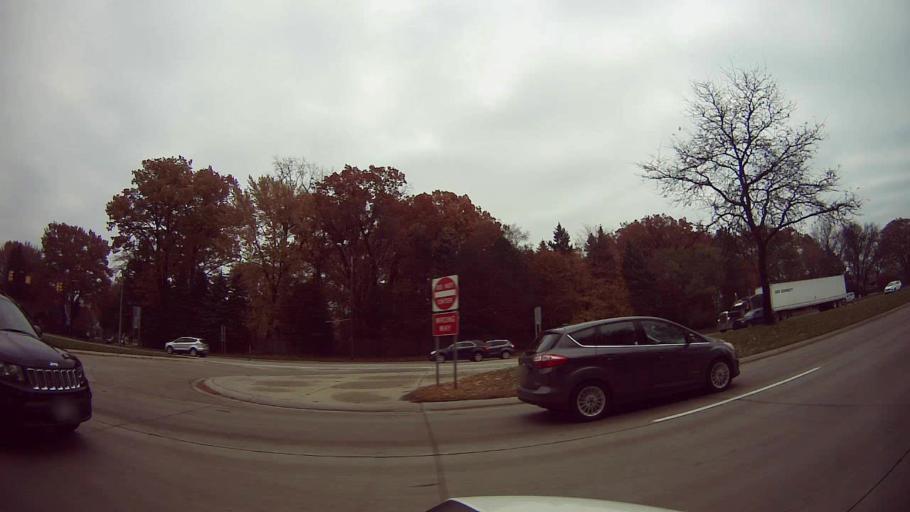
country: US
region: Michigan
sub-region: Wayne County
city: Dearborn Heights
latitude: 42.3055
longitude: -83.2721
